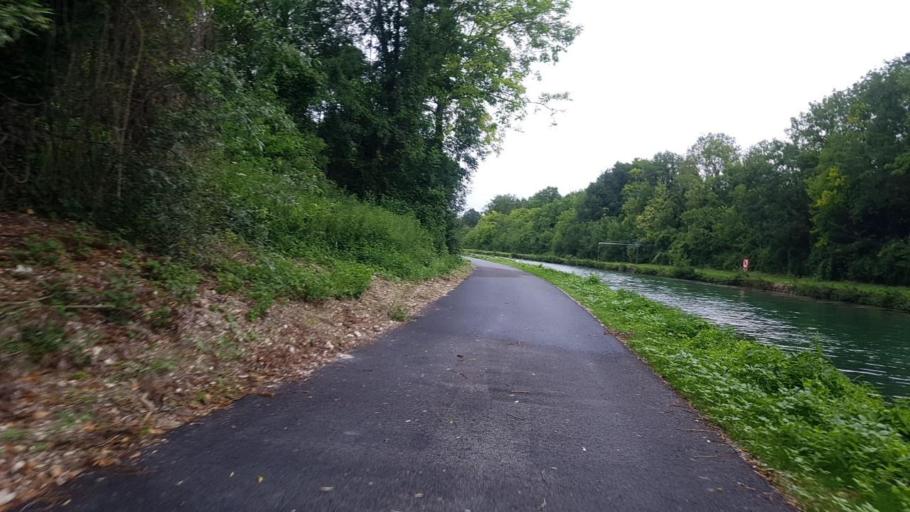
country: FR
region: Champagne-Ardenne
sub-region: Departement de la Marne
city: Vitry-le-Francois
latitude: 48.8362
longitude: 4.5104
